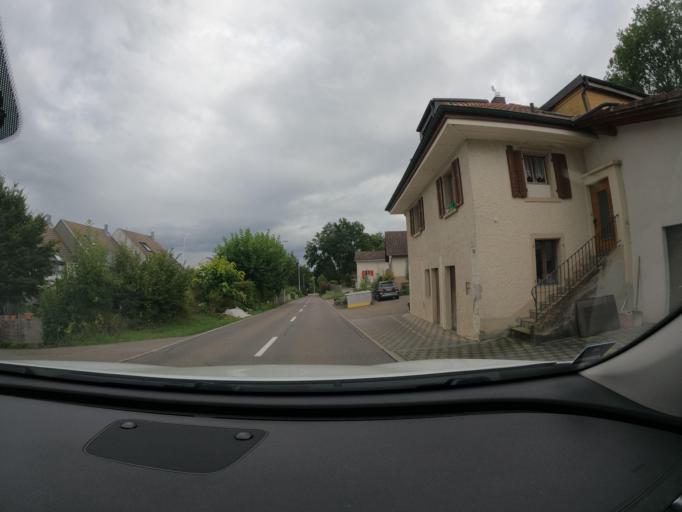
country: CH
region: Aargau
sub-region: Bezirk Kulm
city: Gontenschwil
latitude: 47.2597
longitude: 8.1609
